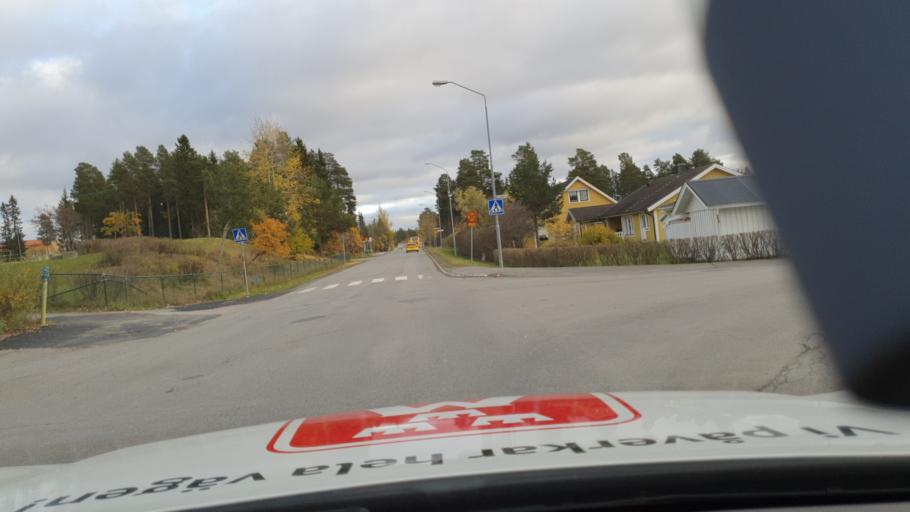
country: SE
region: Jaemtland
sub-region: OEstersunds Kommun
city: Ostersund
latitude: 63.1552
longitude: 14.7469
